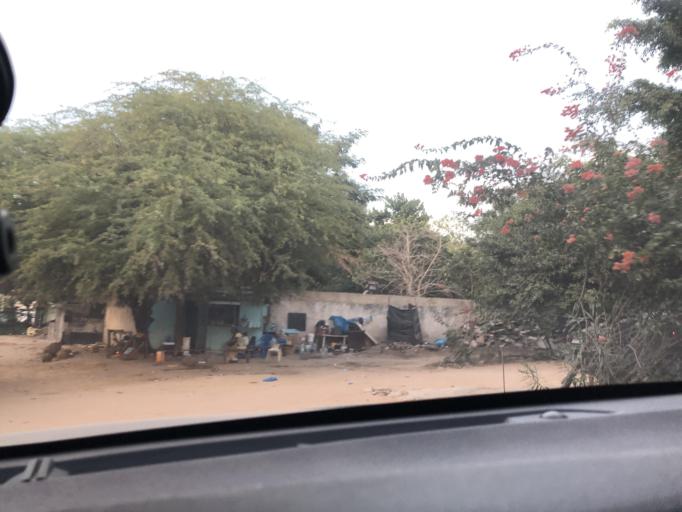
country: SN
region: Dakar
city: Mermoz Boabab
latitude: 14.7389
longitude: -17.5115
